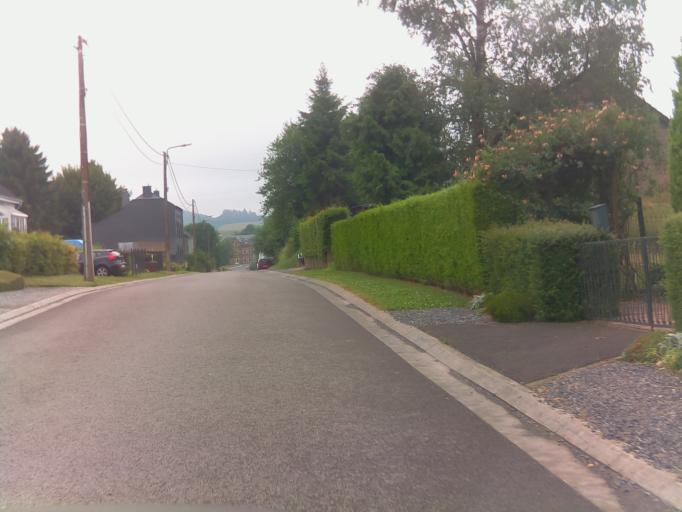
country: BE
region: Wallonia
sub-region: Province du Luxembourg
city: Neufchateau
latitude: 49.8587
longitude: 5.4494
